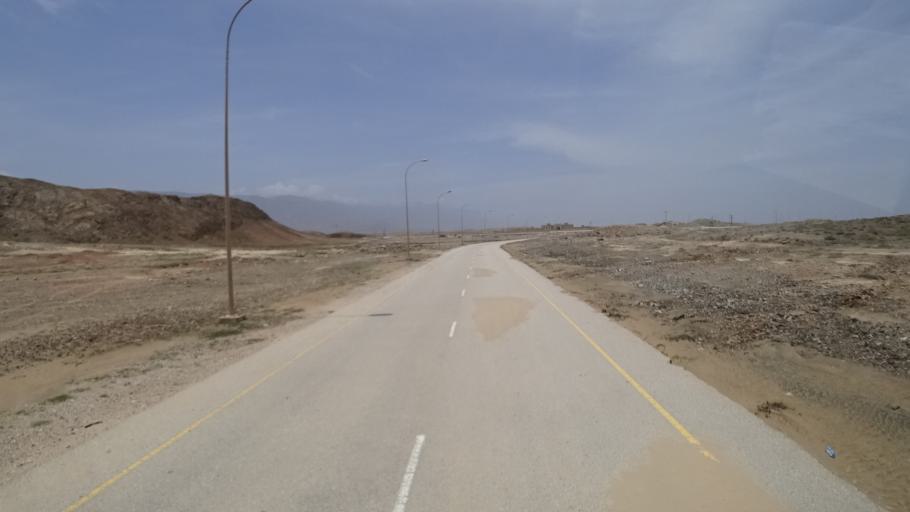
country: OM
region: Zufar
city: Salalah
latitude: 17.0073
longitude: 54.6936
